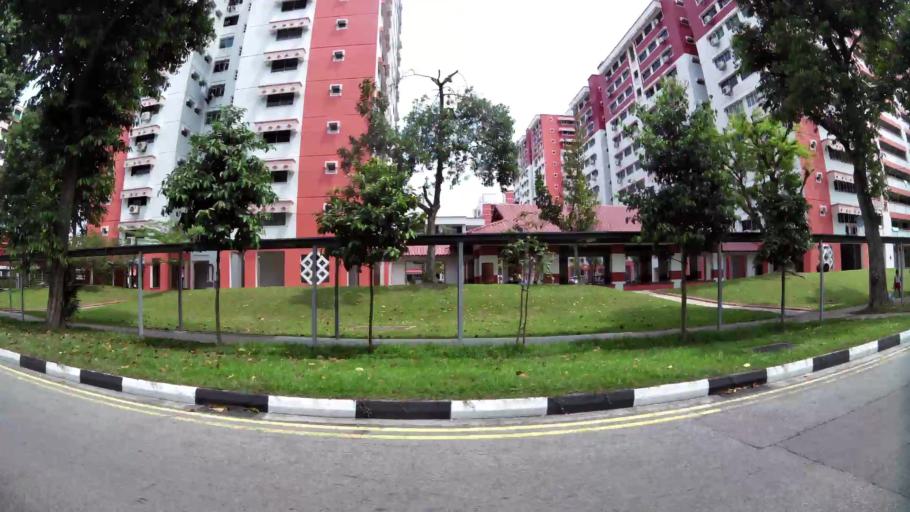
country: MY
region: Johor
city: Johor Bahru
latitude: 1.3832
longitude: 103.7428
